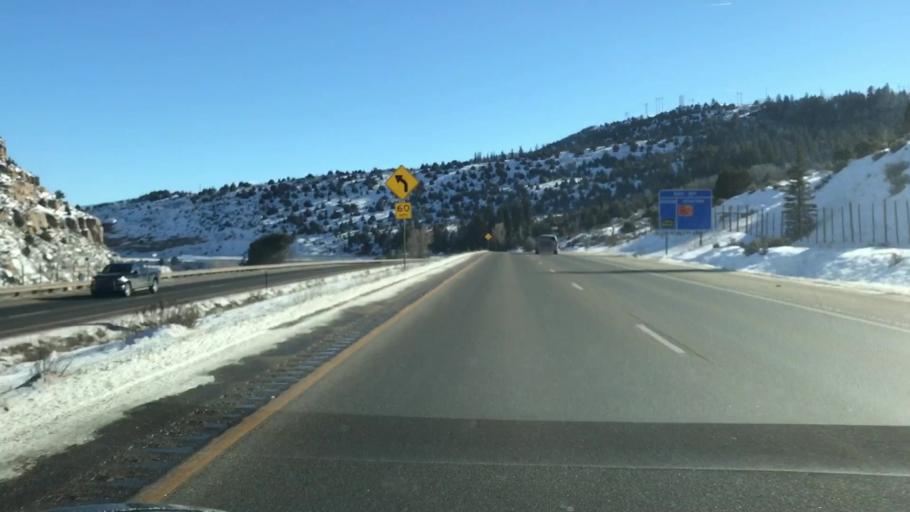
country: US
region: Colorado
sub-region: Eagle County
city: Edwards
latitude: 39.7053
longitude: -106.6902
